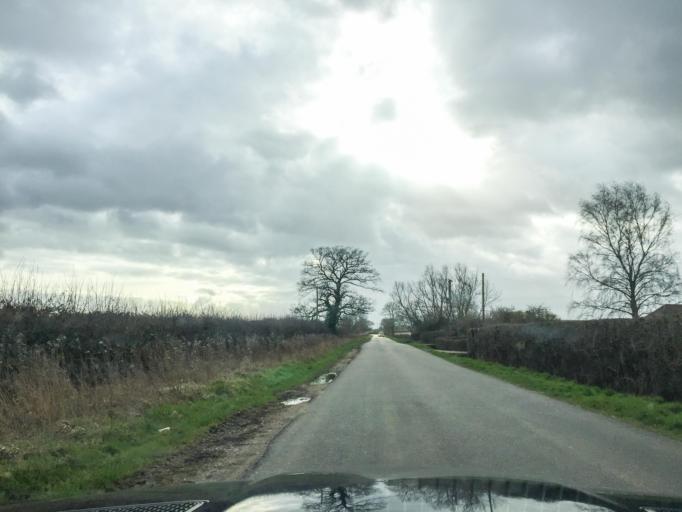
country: GB
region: England
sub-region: Warwickshire
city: Shipston on Stour
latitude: 52.1018
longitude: -1.5697
